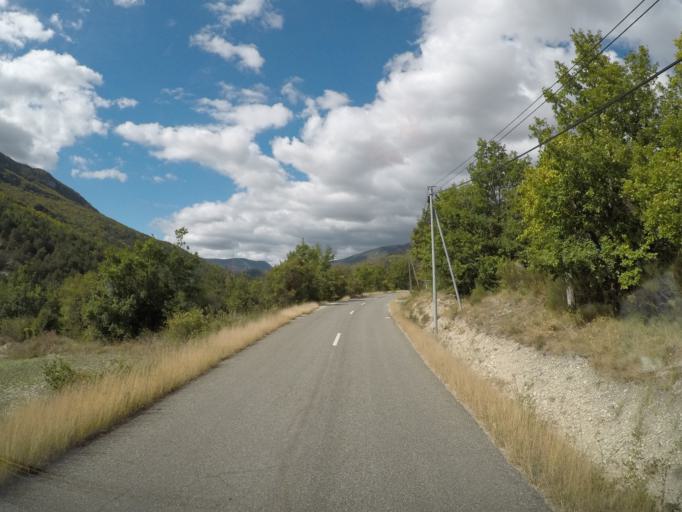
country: FR
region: Provence-Alpes-Cote d'Azur
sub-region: Departement des Hautes-Alpes
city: Laragne-Monteglin
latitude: 44.1756
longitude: 5.6743
